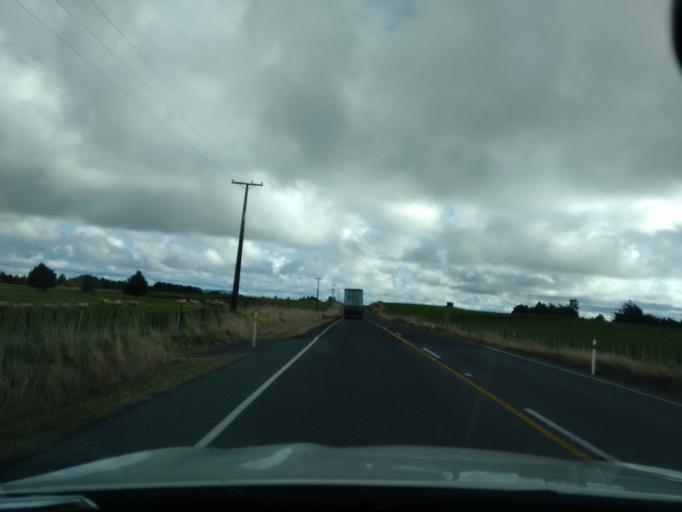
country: NZ
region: Manawatu-Wanganui
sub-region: Ruapehu District
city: Waiouru
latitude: -39.3532
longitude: 175.3577
